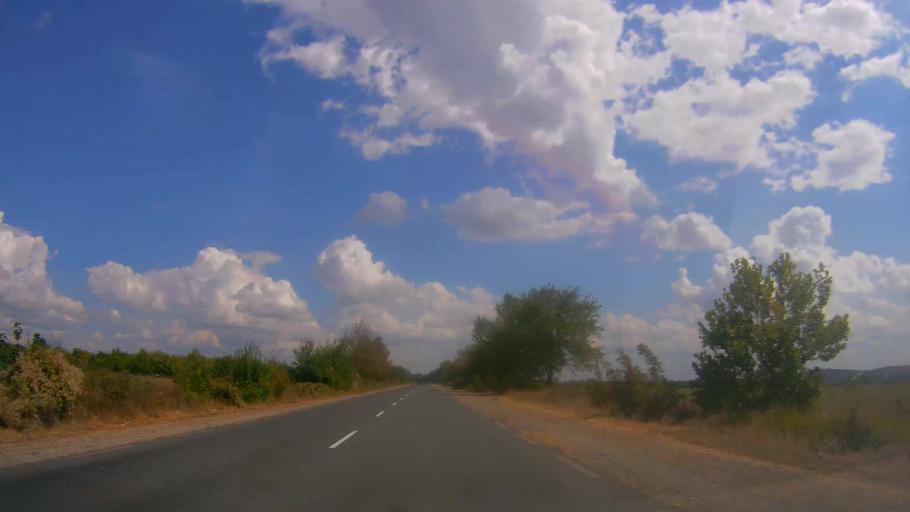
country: BG
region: Sliven
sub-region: Obshtina Sliven
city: Kermen
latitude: 42.6331
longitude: 26.1682
